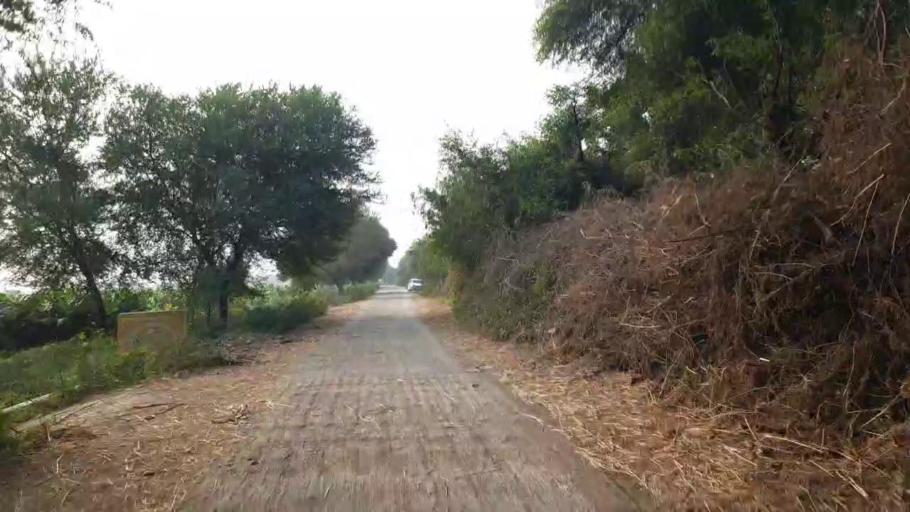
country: PK
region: Sindh
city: Tando Muhammad Khan
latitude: 25.1735
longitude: 68.6063
